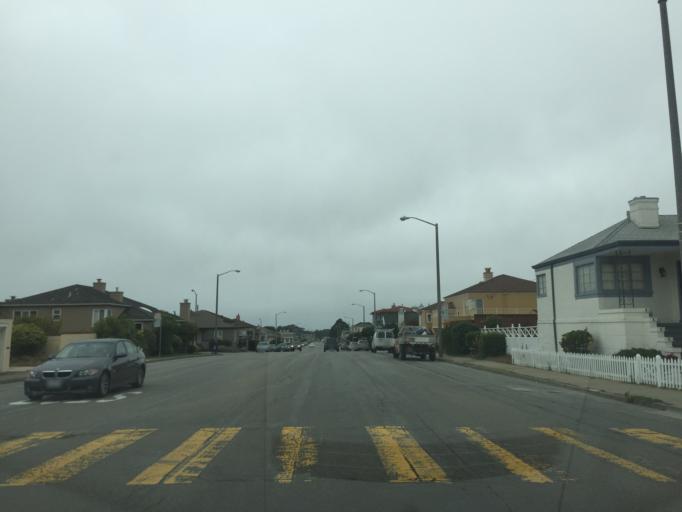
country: US
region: California
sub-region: San Mateo County
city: Daly City
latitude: 37.7324
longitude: -122.4837
